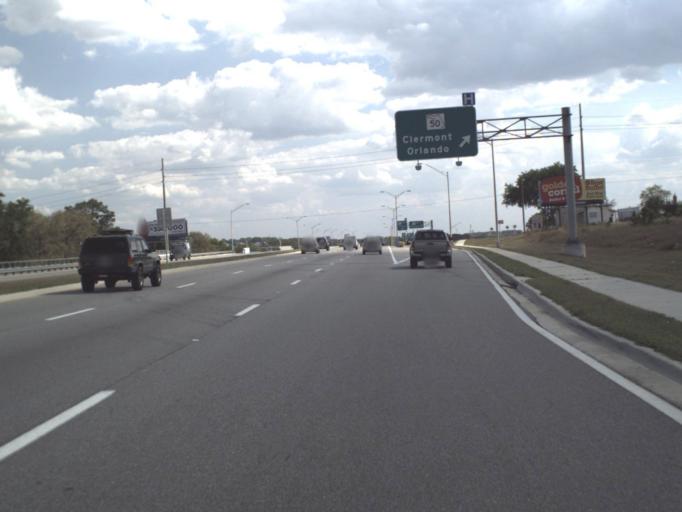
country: US
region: Florida
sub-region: Lake County
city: Minneola
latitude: 28.5526
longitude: -81.7425
